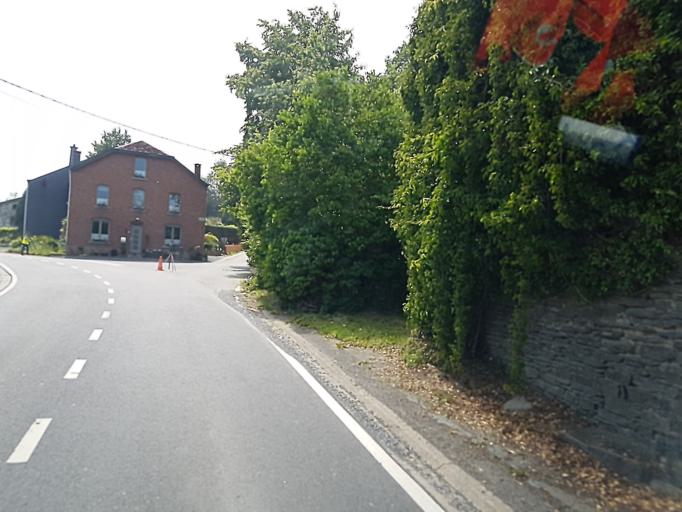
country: BE
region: Wallonia
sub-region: Province du Luxembourg
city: Manhay
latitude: 50.3233
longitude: 5.7322
